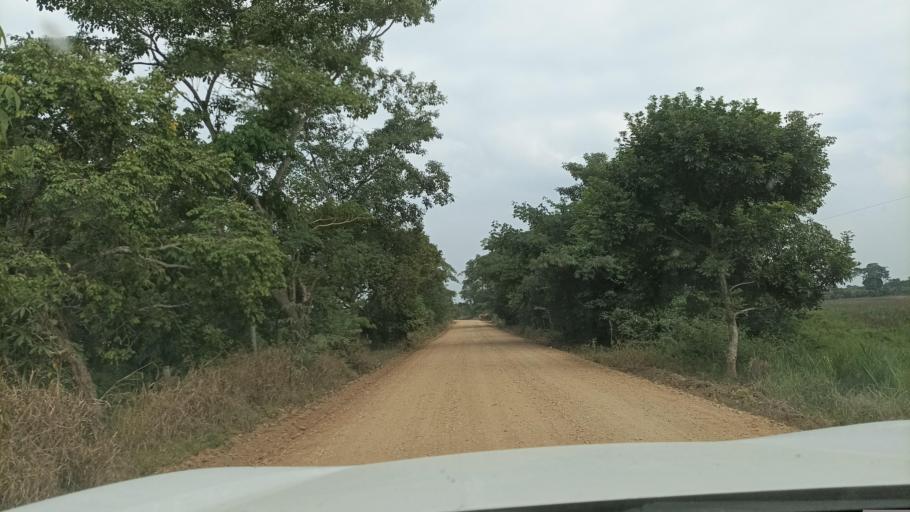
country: MX
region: Veracruz
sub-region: Texistepec
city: San Lorenzo Tenochtitlan
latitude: 17.7742
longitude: -94.8011
